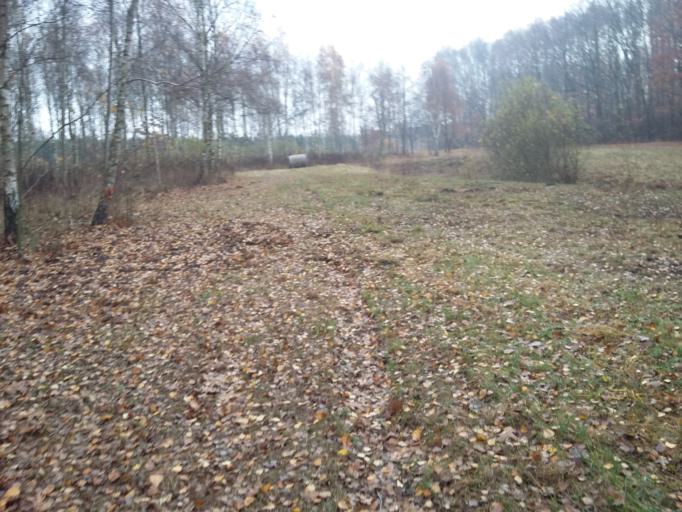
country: PL
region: Lodz Voivodeship
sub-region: Powiat pabianicki
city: Ksawerow
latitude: 51.7293
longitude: 19.3907
